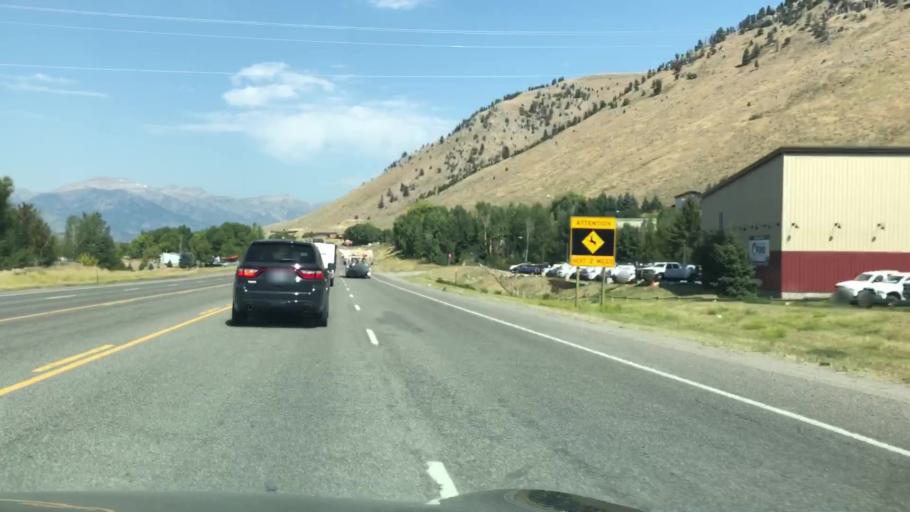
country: US
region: Wyoming
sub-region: Teton County
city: South Park
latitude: 43.4239
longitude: -110.7772
